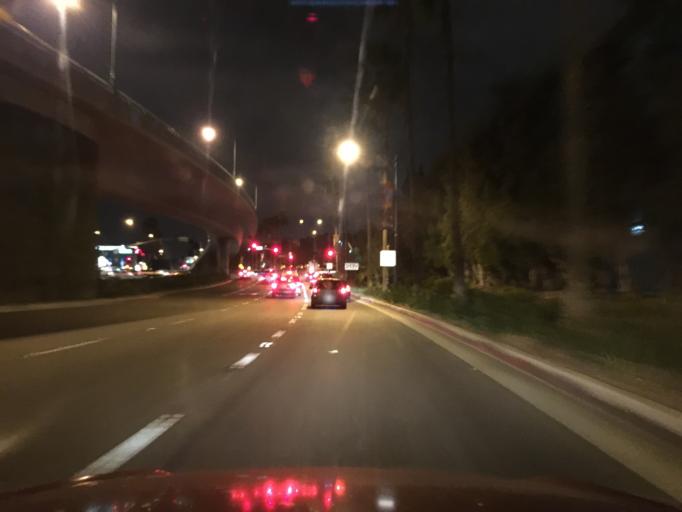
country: US
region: California
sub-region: Orange County
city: Anaheim
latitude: 33.8171
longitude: -117.9220
